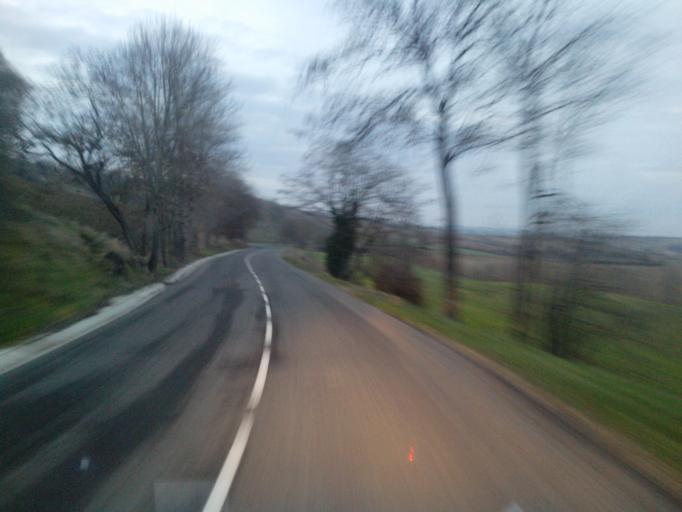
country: FR
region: Languedoc-Roussillon
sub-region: Departement de l'Aude
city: Belpech
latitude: 43.2642
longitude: 1.7531
